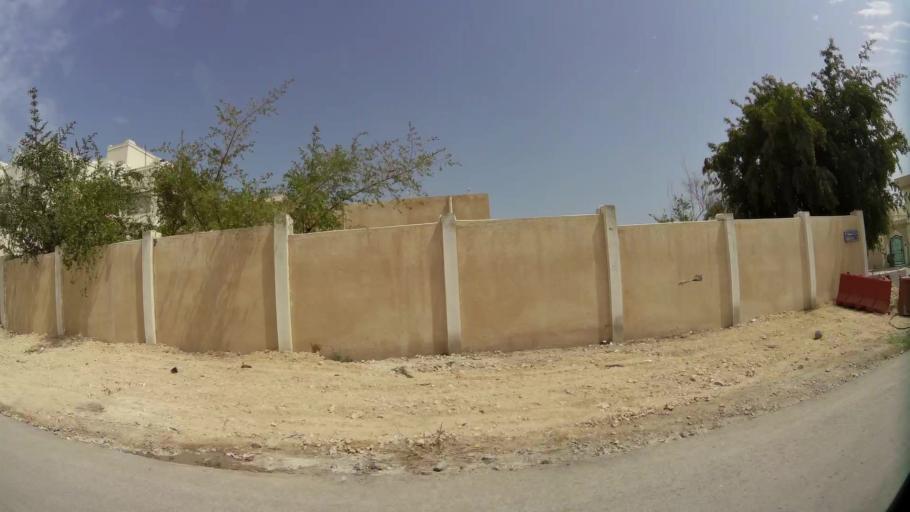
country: QA
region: Baladiyat ar Rayyan
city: Ar Rayyan
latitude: 25.3554
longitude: 51.4740
